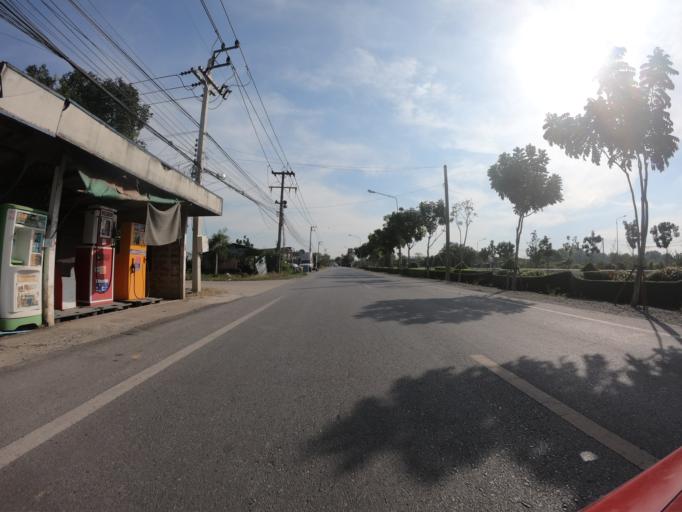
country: TH
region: Pathum Thani
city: Thanyaburi
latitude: 13.9906
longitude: 100.7300
